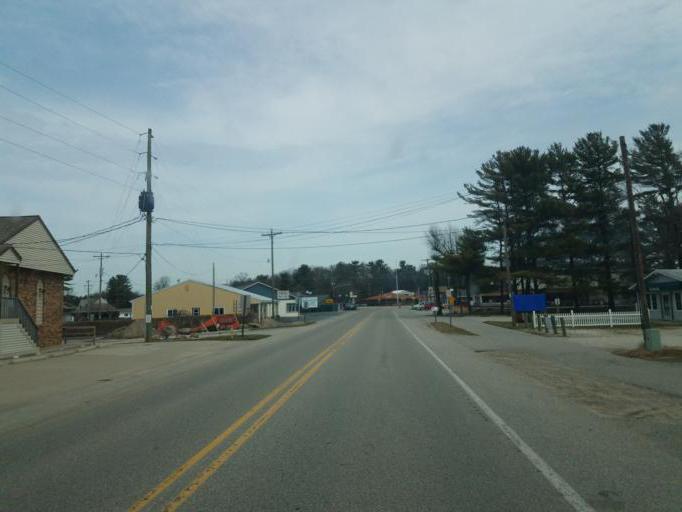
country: US
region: Michigan
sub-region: Oceana County
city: Hart
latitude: 43.6663
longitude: -86.4897
